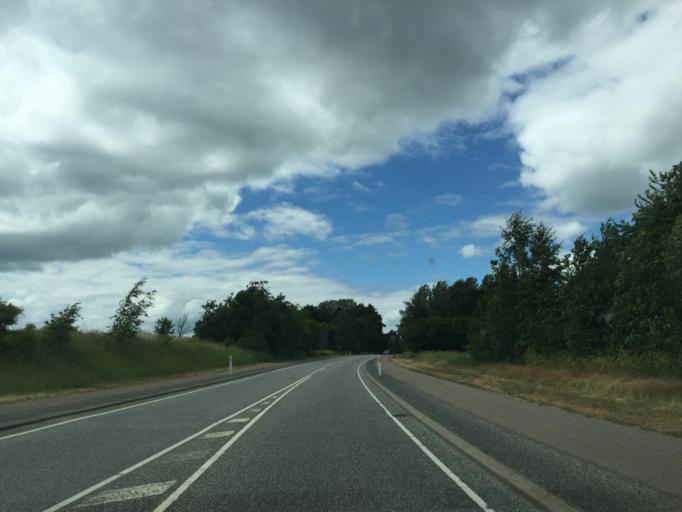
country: DK
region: South Denmark
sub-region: Svendborg Kommune
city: Svendborg
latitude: 55.0711
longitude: 10.5674
